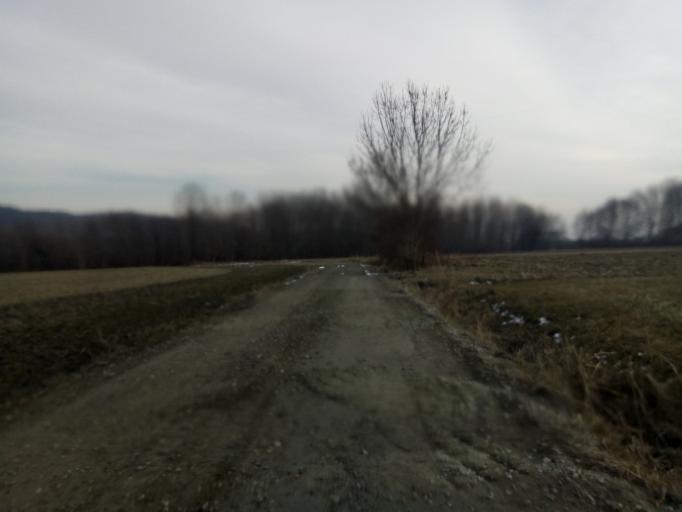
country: IT
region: Piedmont
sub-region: Provincia di Torino
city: Burolo
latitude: 45.4830
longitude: 7.9220
